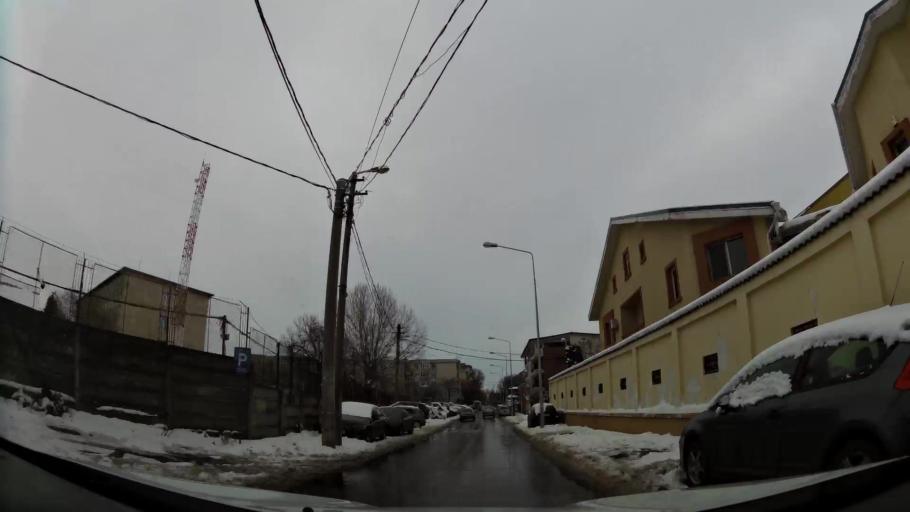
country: RO
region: Bucuresti
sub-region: Municipiul Bucuresti
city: Bucuresti
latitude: 44.3945
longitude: 26.1127
